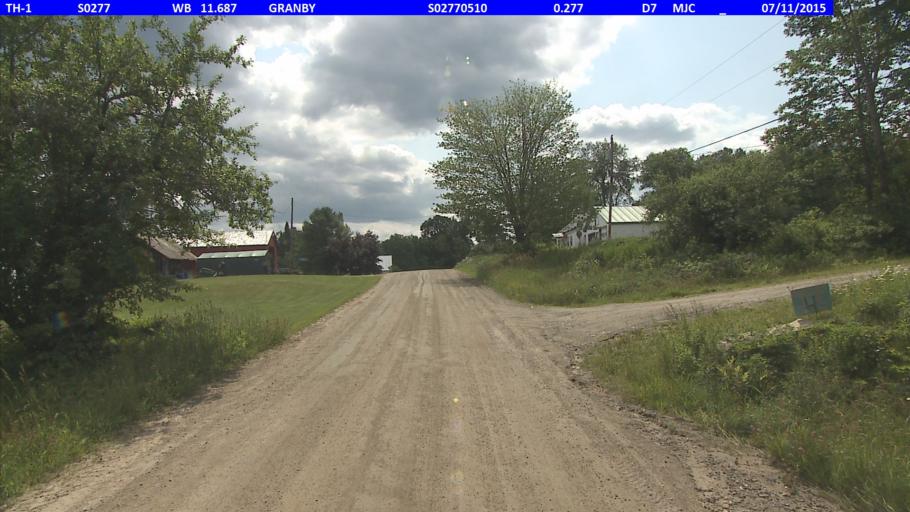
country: US
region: Vermont
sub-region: Essex County
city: Guildhall
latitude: 44.5710
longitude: -71.7571
